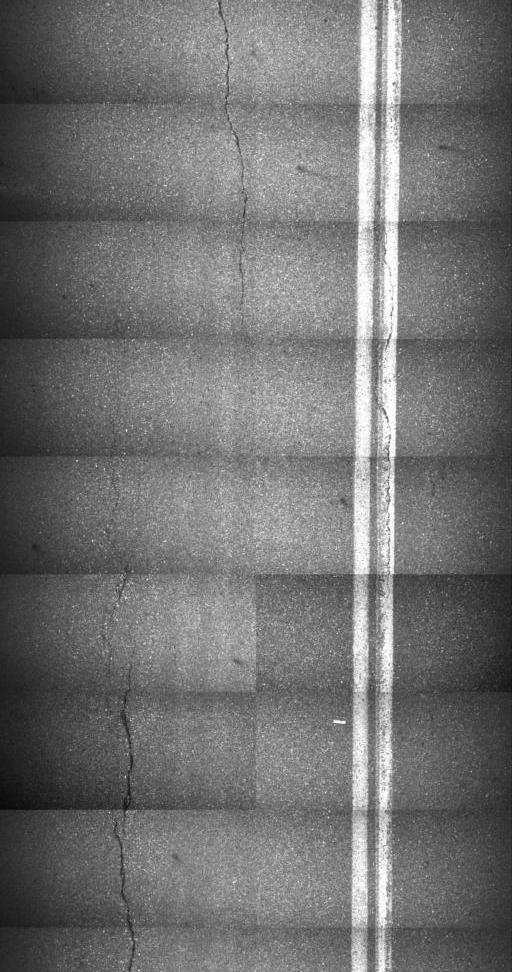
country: US
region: Vermont
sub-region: Washington County
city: Northfield
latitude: 44.0439
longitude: -72.6462
